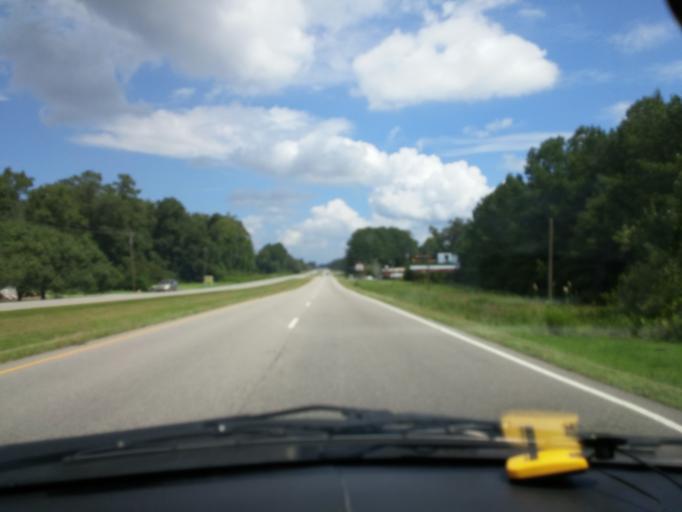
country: US
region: North Carolina
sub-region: Pitt County
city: Grifton
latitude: 35.3293
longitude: -77.4906
